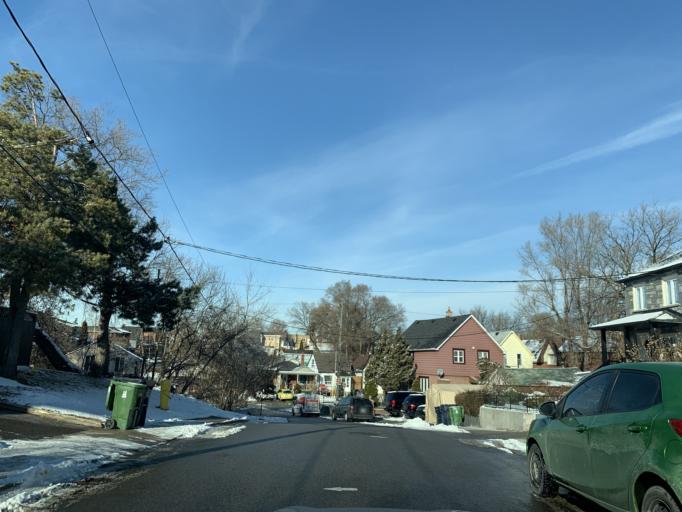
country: CA
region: Ontario
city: Toronto
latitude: 43.6805
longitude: -79.4691
